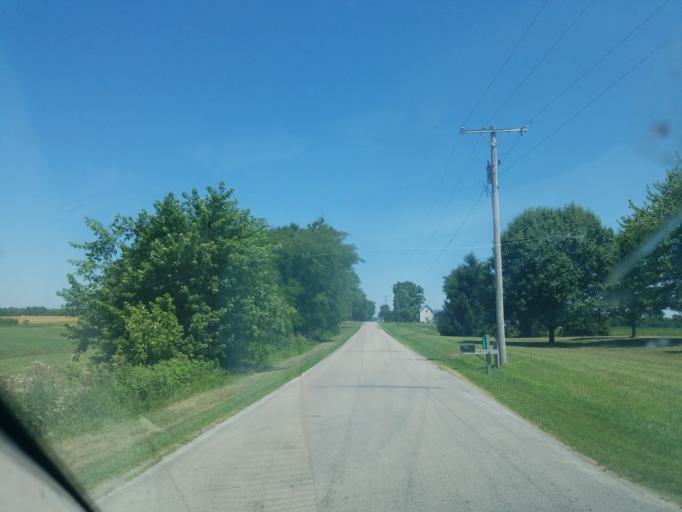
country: US
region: Ohio
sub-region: Mercer County
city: Rockford
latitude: 40.7280
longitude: -84.7370
